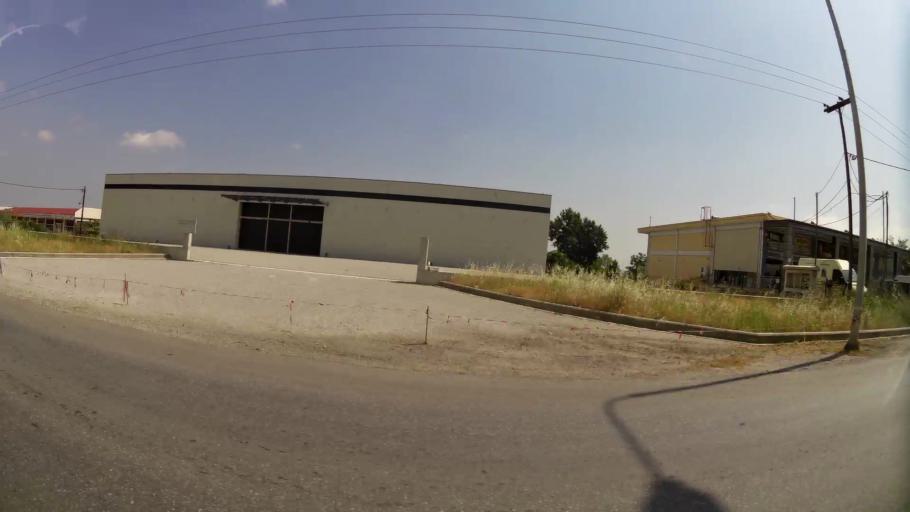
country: GR
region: Central Macedonia
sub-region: Nomos Imathias
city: Veroia
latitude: 40.5126
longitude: 22.2147
